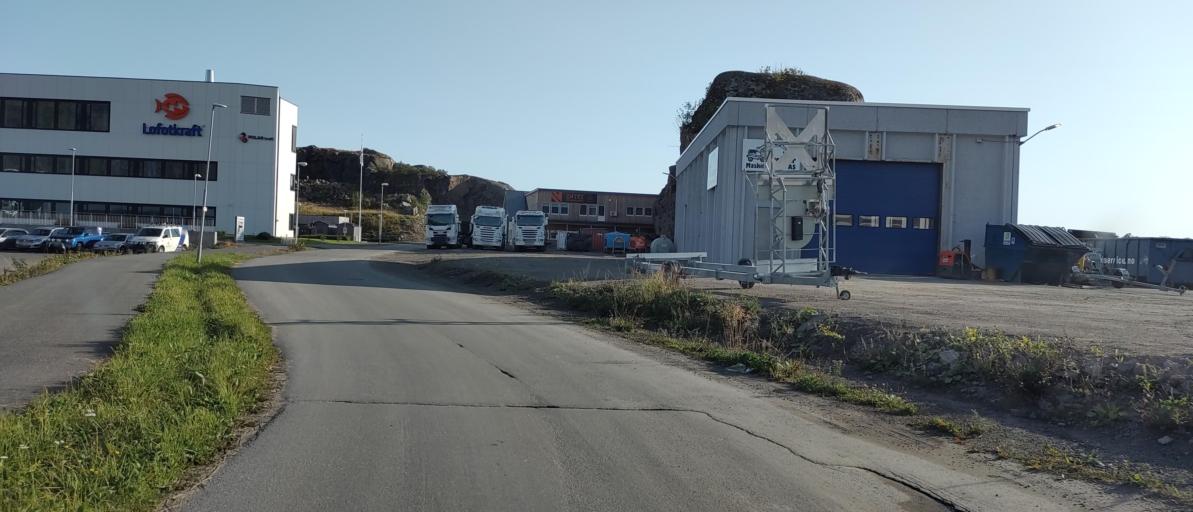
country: NO
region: Nordland
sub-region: Vagan
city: Svolvaer
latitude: 68.2261
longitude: 14.5550
